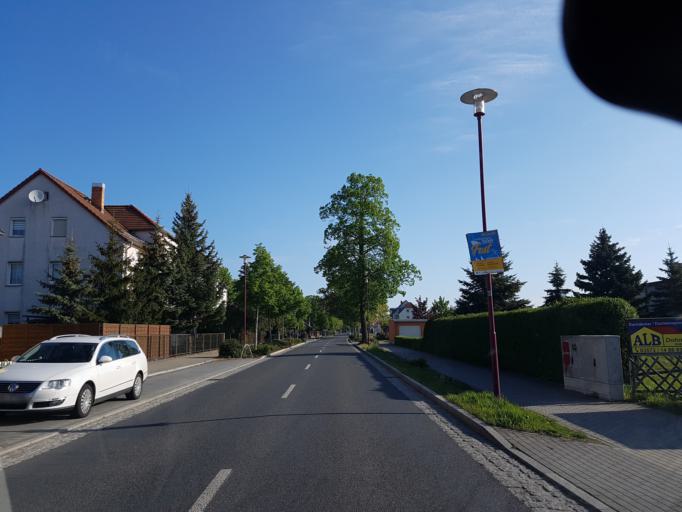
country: DE
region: Brandenburg
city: Grossraschen
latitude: 51.5895
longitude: 14.0114
